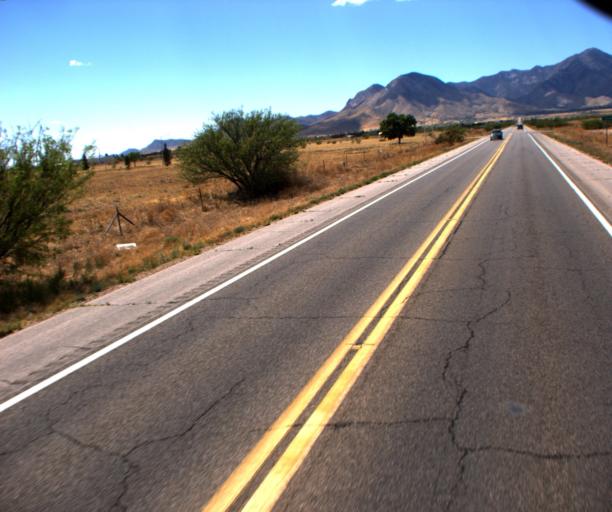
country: US
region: Arizona
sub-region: Cochise County
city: Sierra Vista Southeast
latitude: 31.3800
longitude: -110.1544
